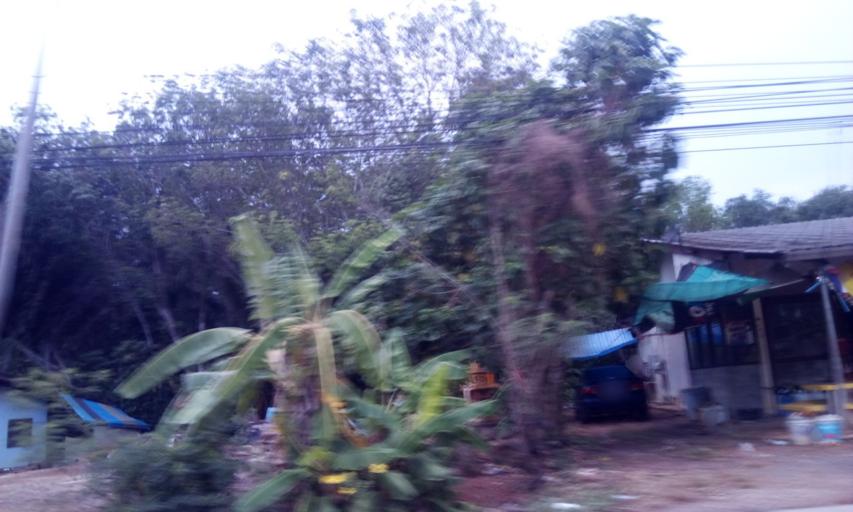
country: TH
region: Trat
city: Khao Saming
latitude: 12.2891
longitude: 102.3176
